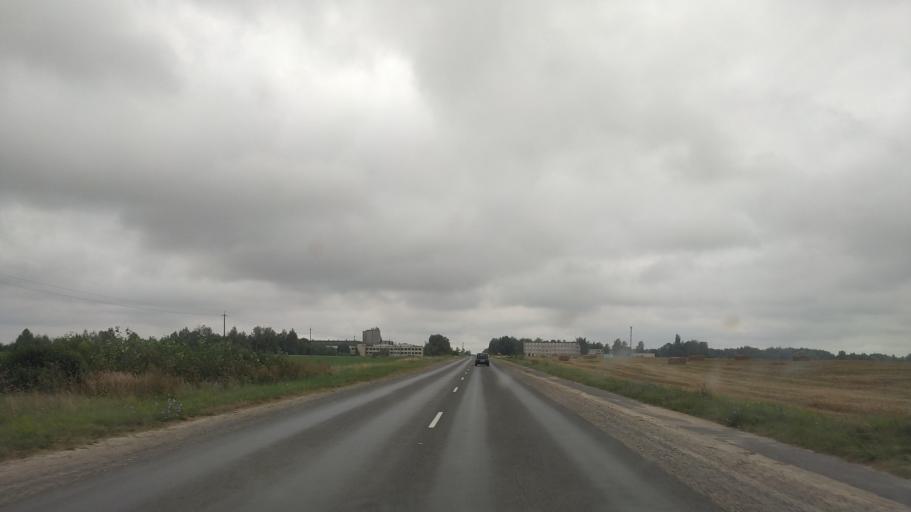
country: BY
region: Brest
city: Byaroza
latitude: 52.5487
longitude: 24.9469
